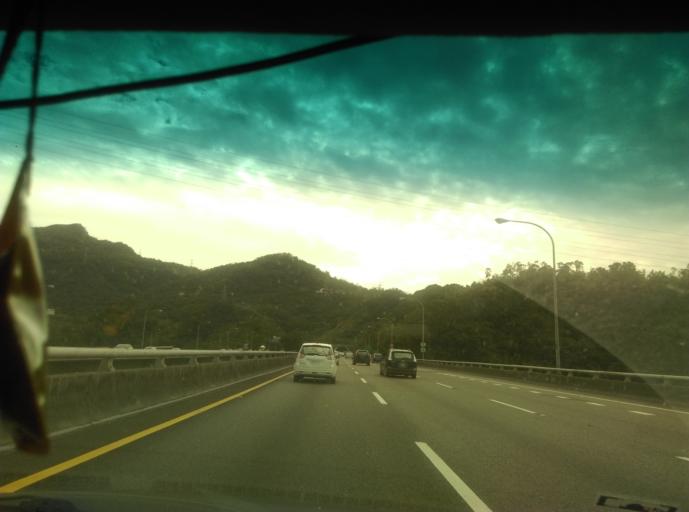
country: TW
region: Taipei
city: Taipei
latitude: 24.9980
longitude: 121.5939
